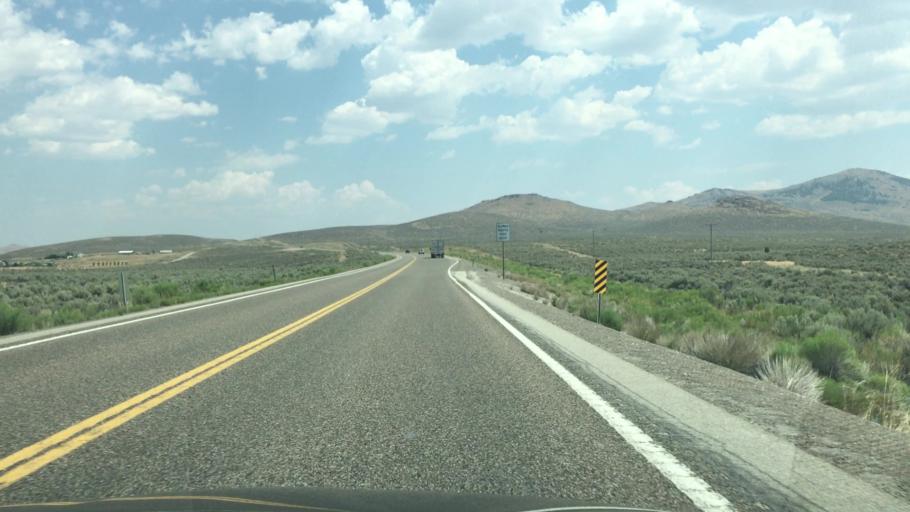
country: US
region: Nevada
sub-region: Elko County
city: Wells
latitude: 41.1698
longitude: -114.8839
